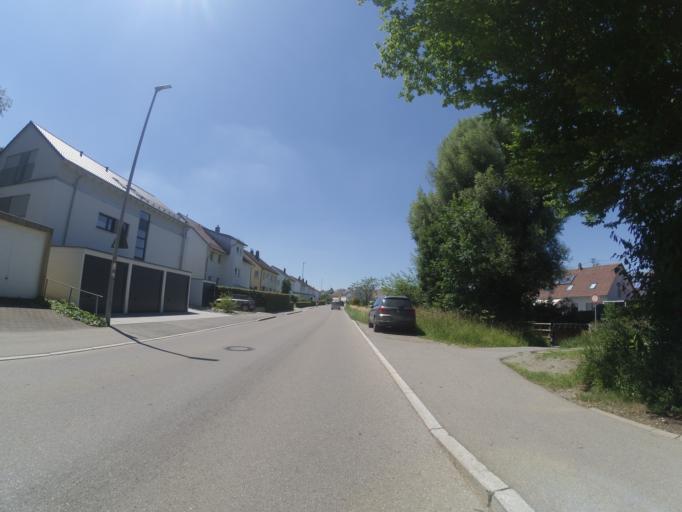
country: DE
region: Baden-Wuerttemberg
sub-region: Tuebingen Region
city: Bad Waldsee
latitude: 47.9199
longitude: 9.7428
